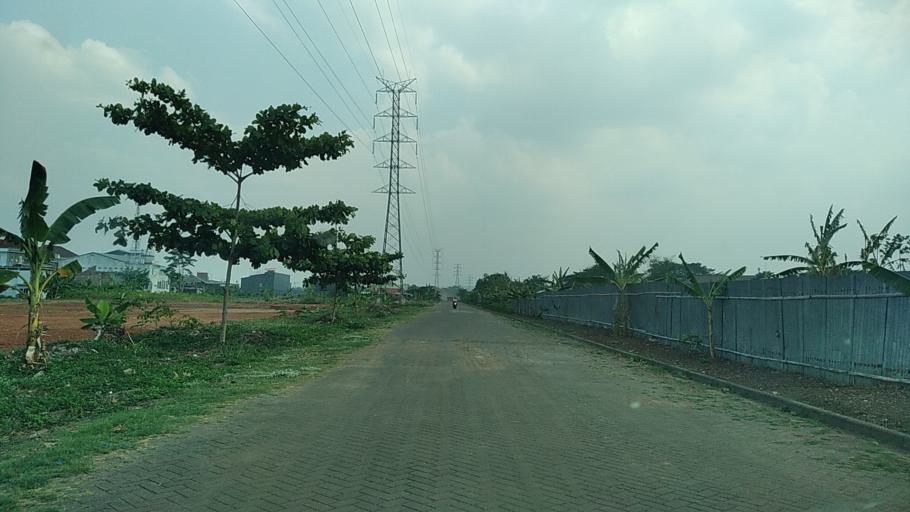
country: ID
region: Central Java
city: Semarang
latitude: -7.0600
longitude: 110.4342
